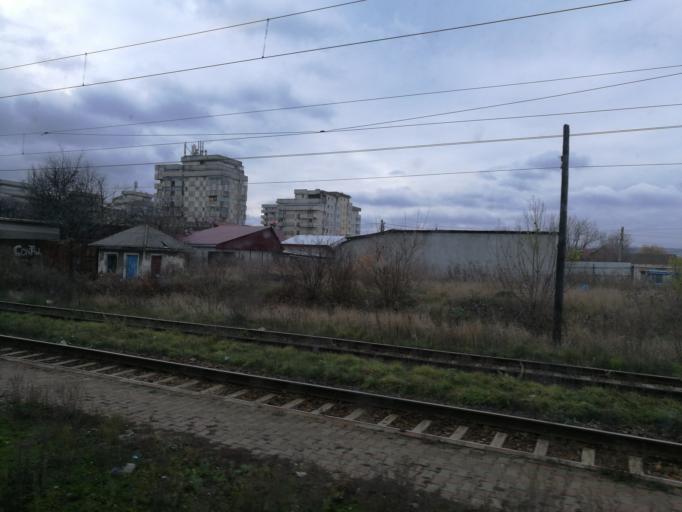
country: RO
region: Iasi
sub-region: Municipiul Pascani
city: Pascani
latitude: 47.2583
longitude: 26.7235
